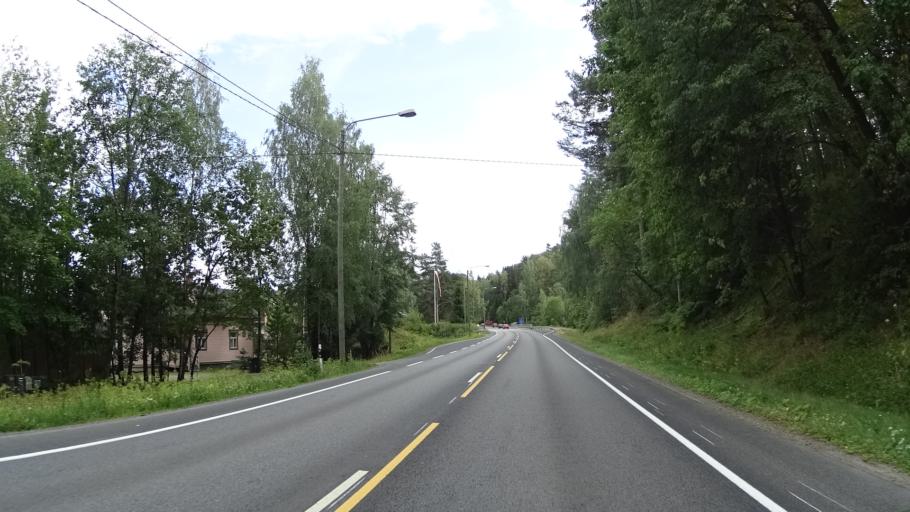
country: FI
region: Pirkanmaa
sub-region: Tampere
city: Kangasala
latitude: 61.4218
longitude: 24.1403
